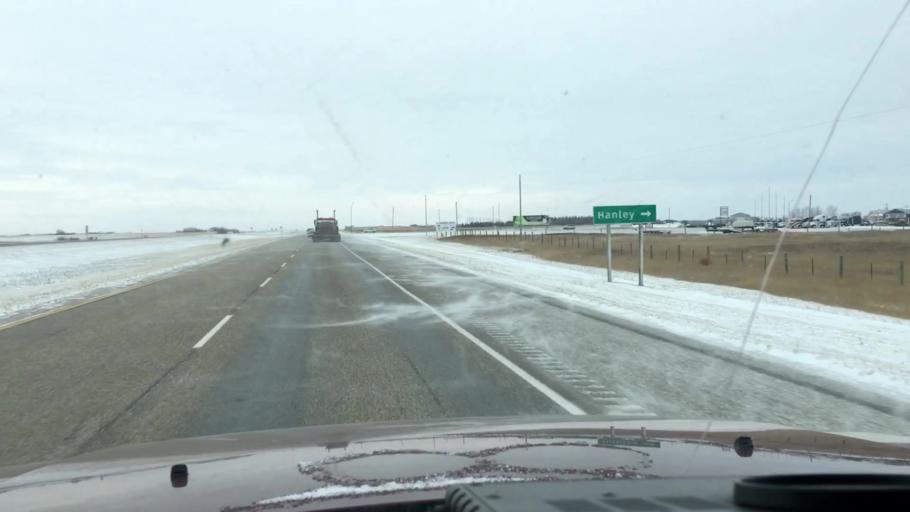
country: CA
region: Saskatchewan
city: Saskatoon
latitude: 51.6357
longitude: -106.4304
